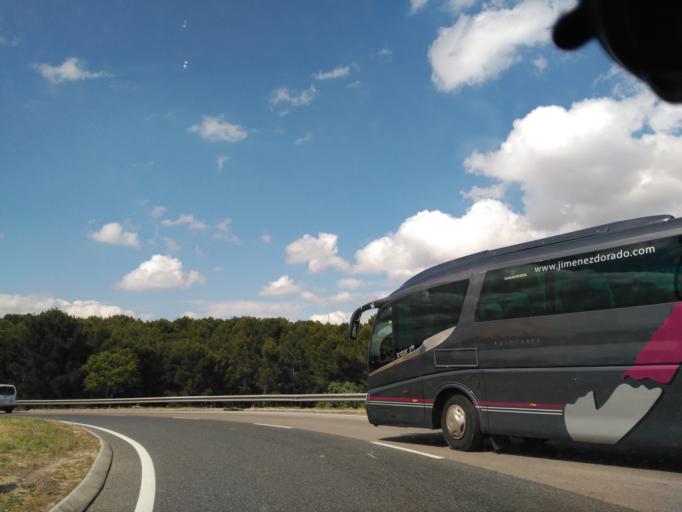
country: ES
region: Madrid
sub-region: Provincia de Madrid
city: Getafe
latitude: 40.3034
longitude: -3.6896
